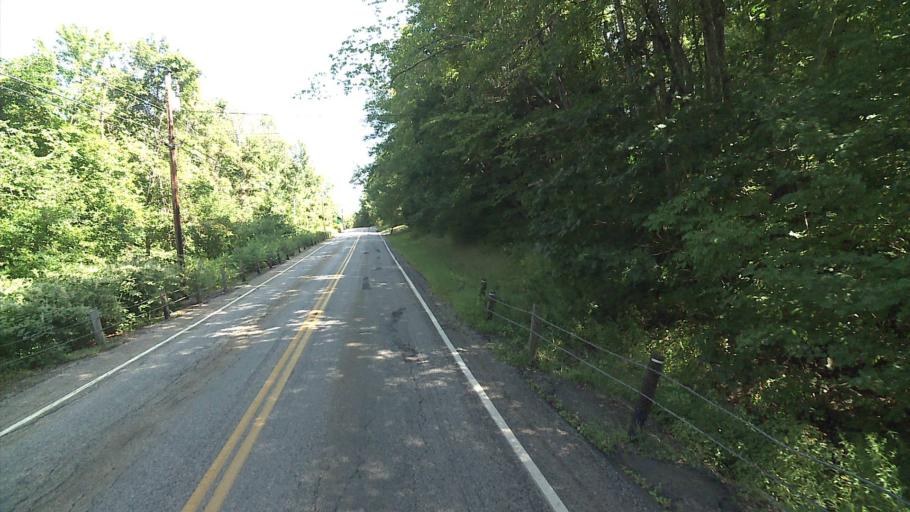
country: US
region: Connecticut
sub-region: Litchfield County
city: Plymouth
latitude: 41.6980
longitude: -73.0568
